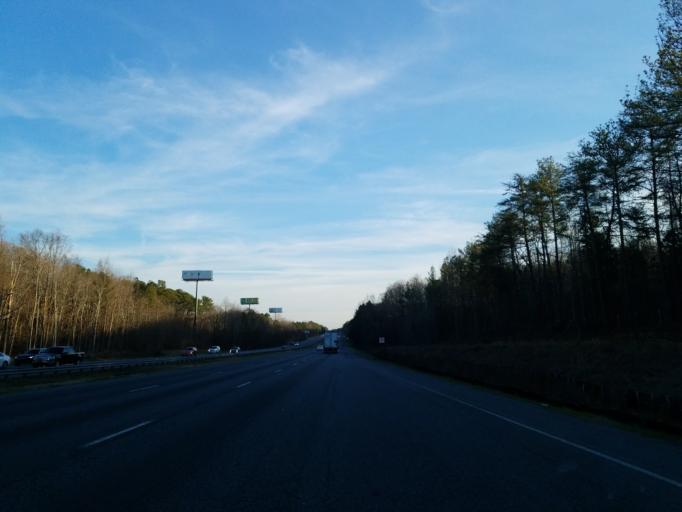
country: US
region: Georgia
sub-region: Whitfield County
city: Dalton
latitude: 34.6504
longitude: -84.9829
